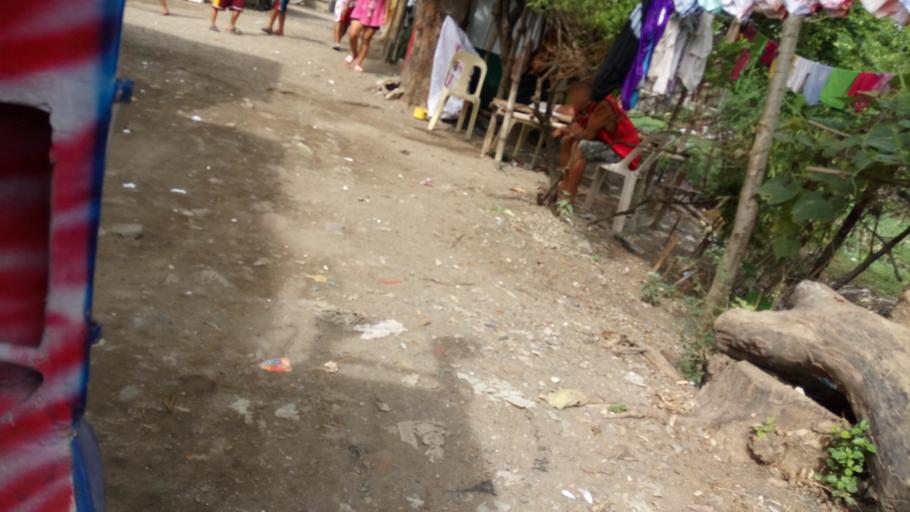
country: PH
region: Ilocos
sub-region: Province of La Union
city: Aringay
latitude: 16.3985
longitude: 120.3519
